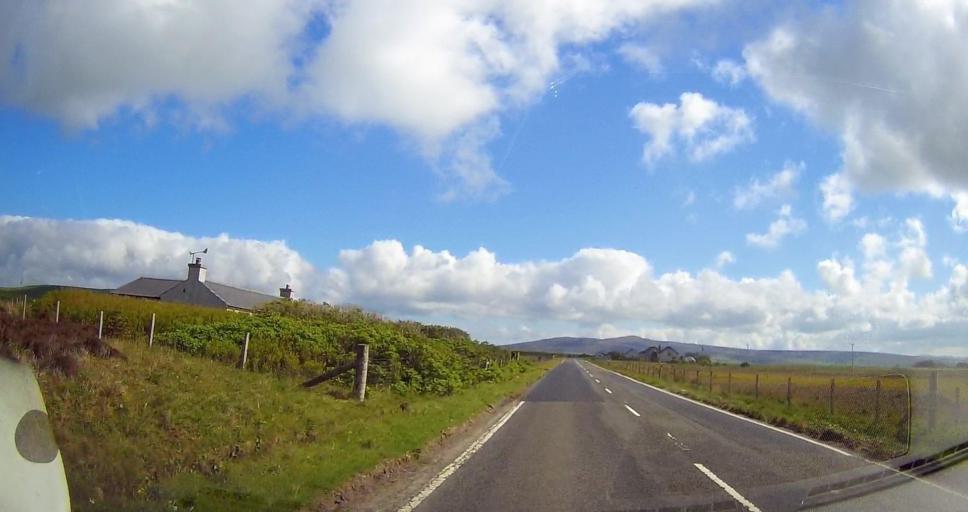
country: GB
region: Scotland
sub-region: Orkney Islands
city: Stromness
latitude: 59.0147
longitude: -3.1561
